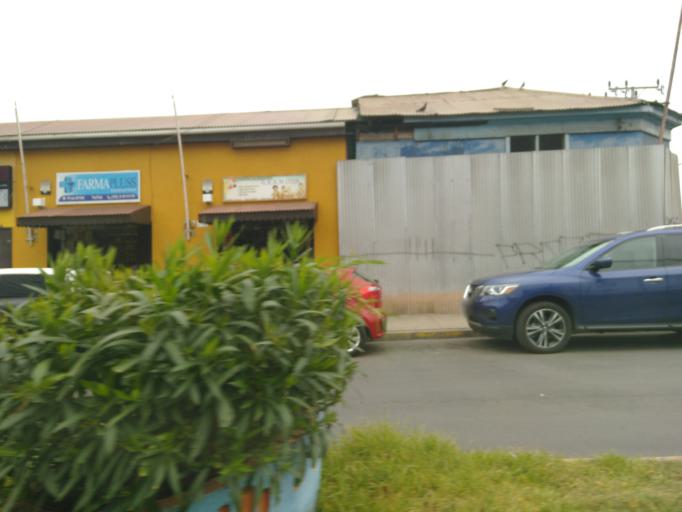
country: CL
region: Antofagasta
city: Taltal
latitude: -25.4061
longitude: -70.4836
